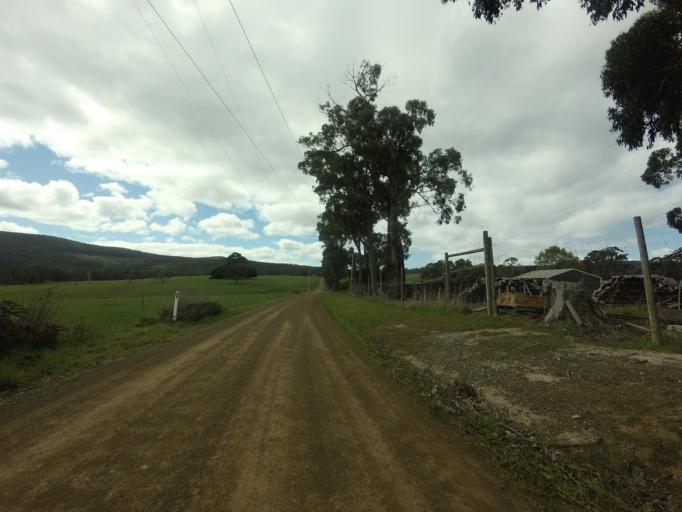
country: AU
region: Tasmania
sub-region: Huon Valley
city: Geeveston
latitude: -43.4342
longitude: 146.9872
